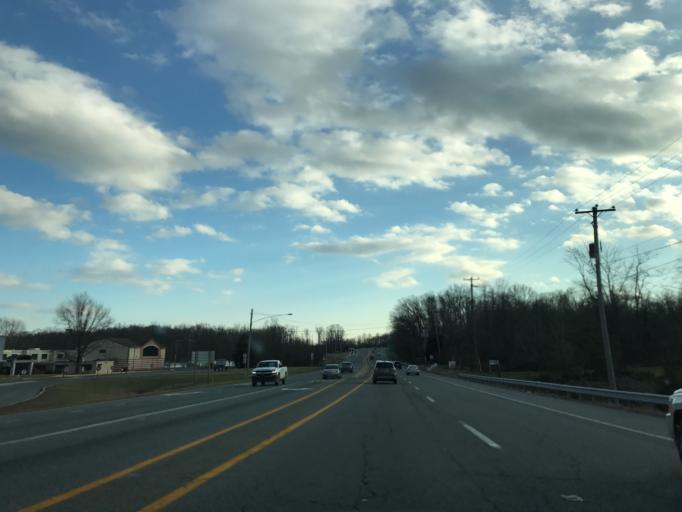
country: US
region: Maryland
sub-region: Cecil County
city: North East
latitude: 39.6402
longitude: -75.9585
